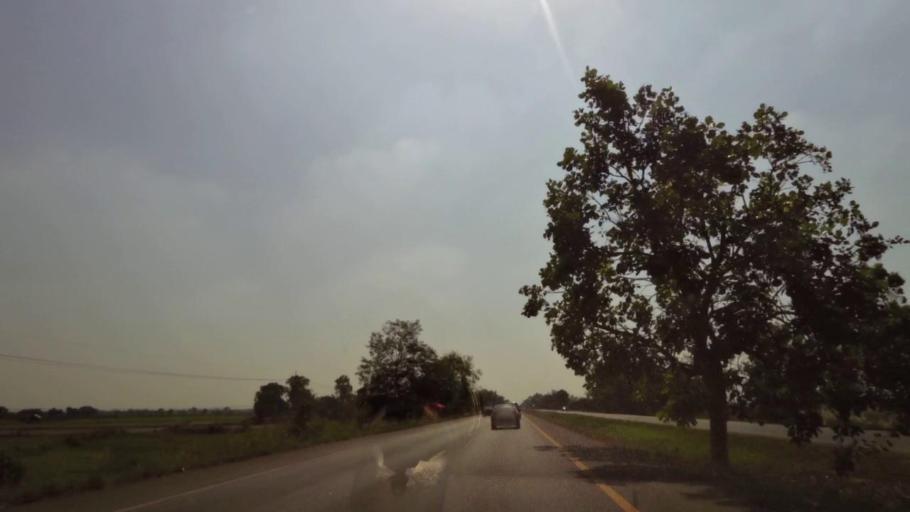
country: TH
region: Phichit
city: Wachira Barami
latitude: 16.4519
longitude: 100.1465
